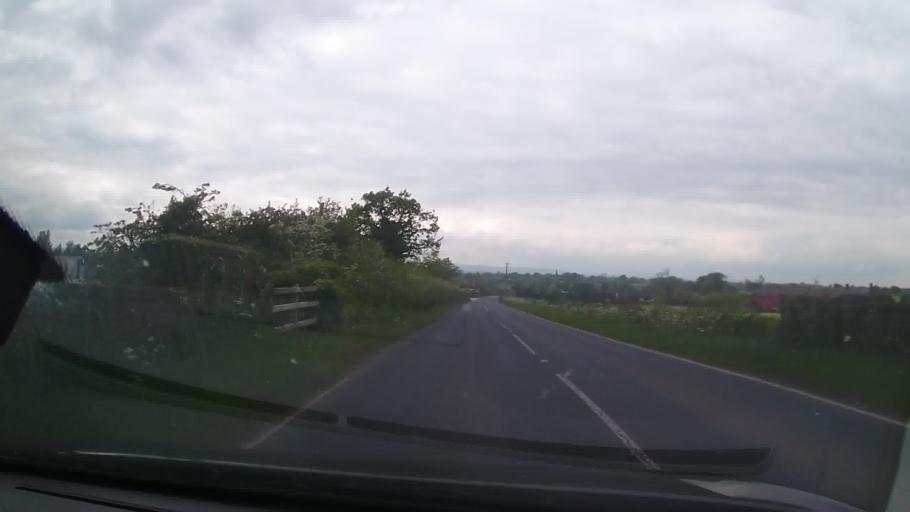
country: GB
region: Wales
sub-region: Wrexham
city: Overton
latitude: 52.9609
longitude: -2.9118
